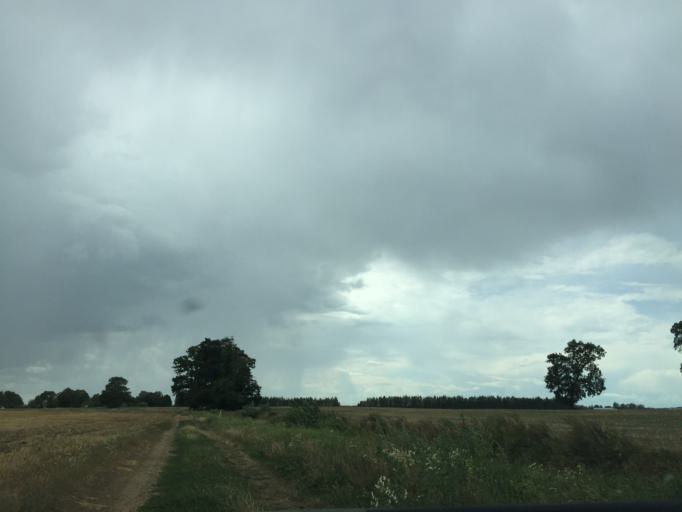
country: LT
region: Siauliu apskritis
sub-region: Joniskis
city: Joniskis
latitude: 56.2924
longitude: 23.7267
